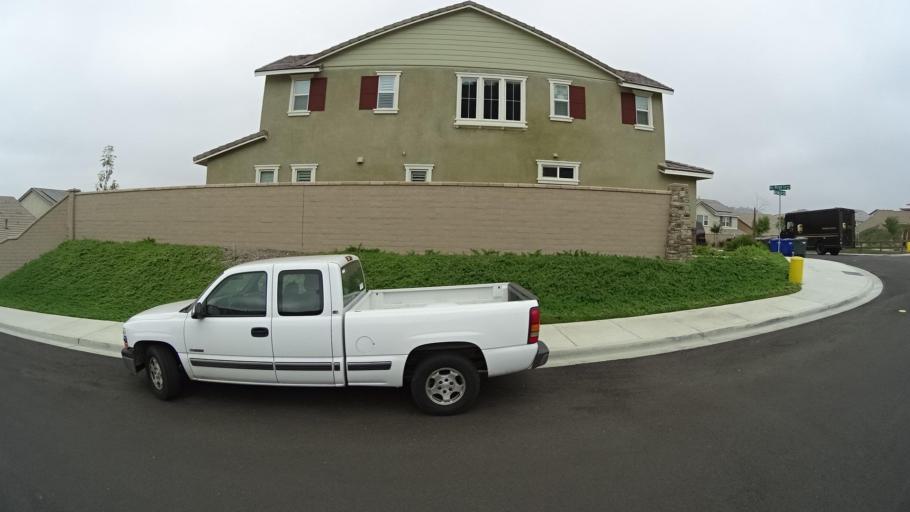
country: US
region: California
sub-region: San Diego County
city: Rainbow
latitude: 33.3563
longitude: -117.1504
